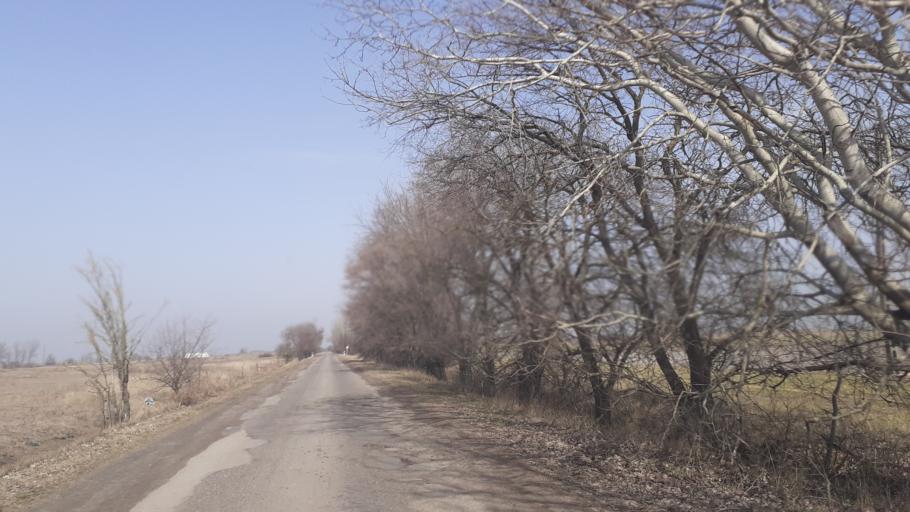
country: HU
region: Pest
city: Dabas
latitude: 47.0691
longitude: 19.2576
